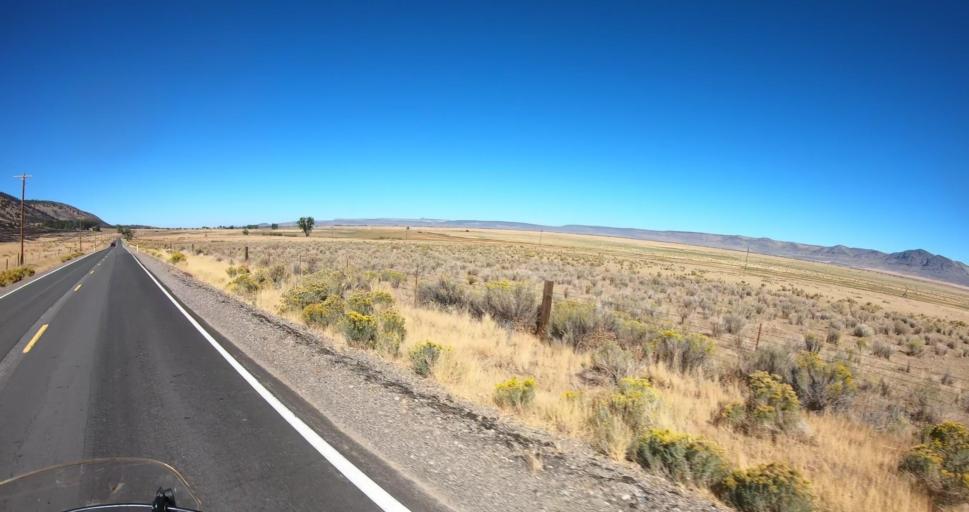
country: US
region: Oregon
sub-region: Lake County
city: Lakeview
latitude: 42.6323
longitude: -120.5129
